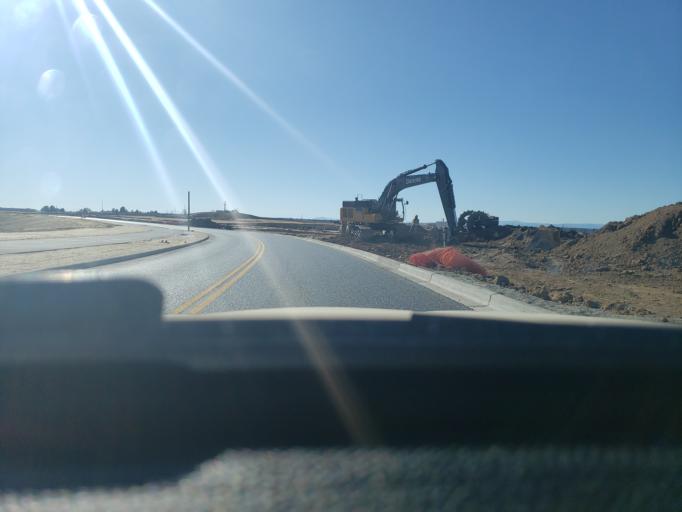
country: US
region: Colorado
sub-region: Adams County
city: Aurora
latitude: 39.7609
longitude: -104.7134
